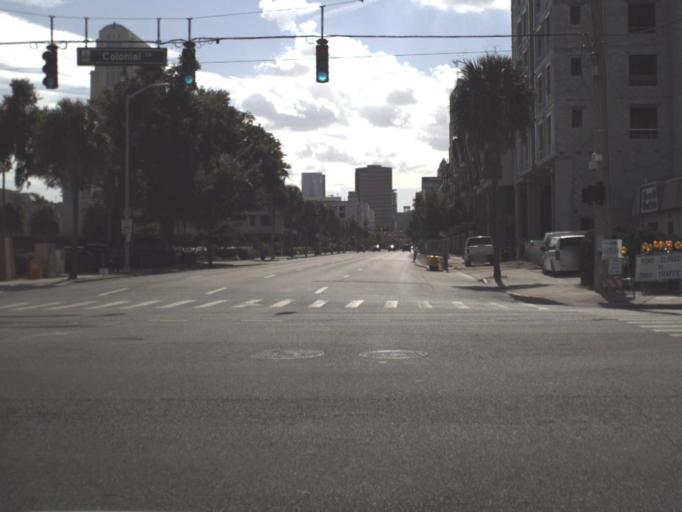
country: US
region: Florida
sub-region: Orange County
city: Orlando
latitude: 28.5532
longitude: -81.3793
